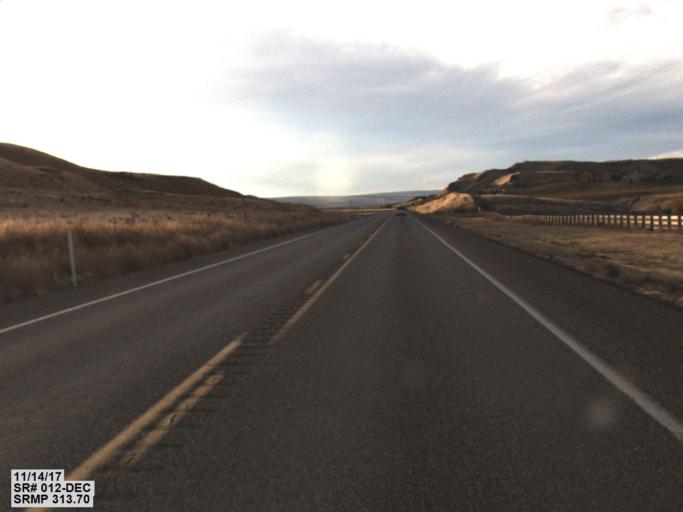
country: US
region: Washington
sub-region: Walla Walla County
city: Burbank
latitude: 46.0725
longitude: -118.7912
